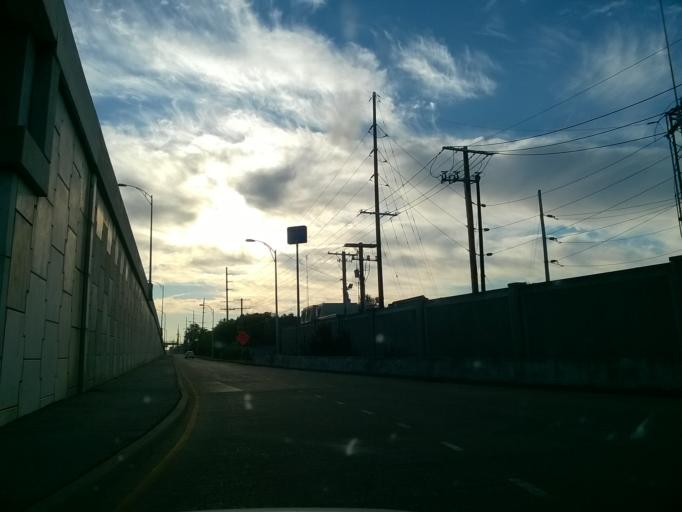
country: US
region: Indiana
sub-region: Vanderburgh County
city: Melody Hill
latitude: 37.9765
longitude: -87.4917
